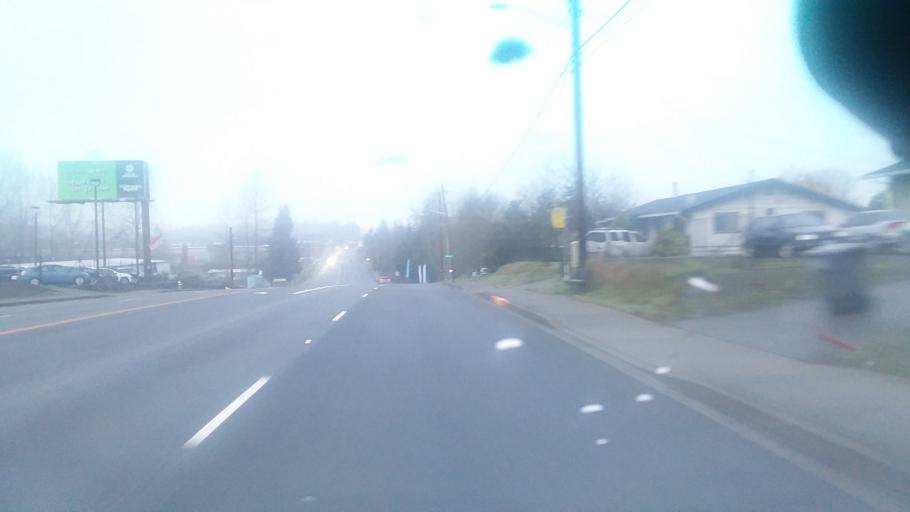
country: US
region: Washington
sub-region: Pierce County
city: Summit
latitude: 47.1549
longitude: -122.3456
